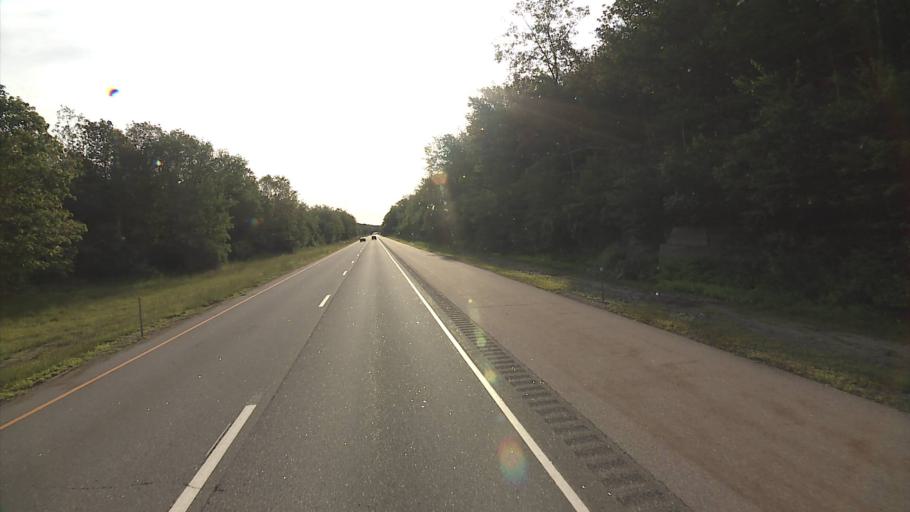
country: US
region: Connecticut
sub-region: New London County
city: Colchester
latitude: 41.5683
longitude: -72.2201
